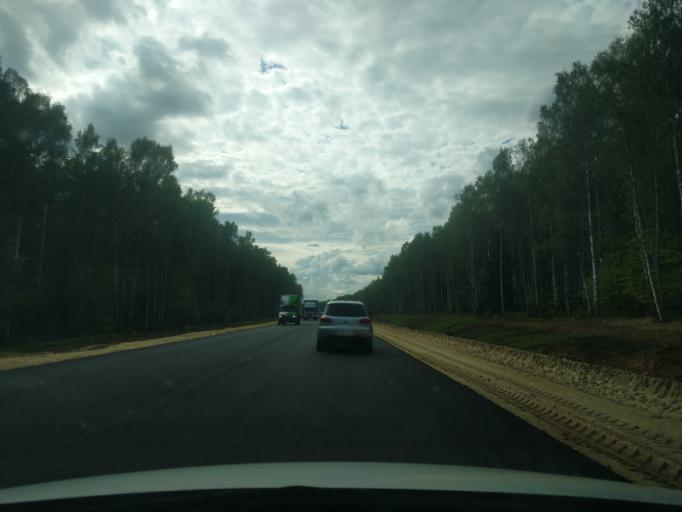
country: RU
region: Jaroslavl
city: Levashevo
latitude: 57.6889
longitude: 40.6186
